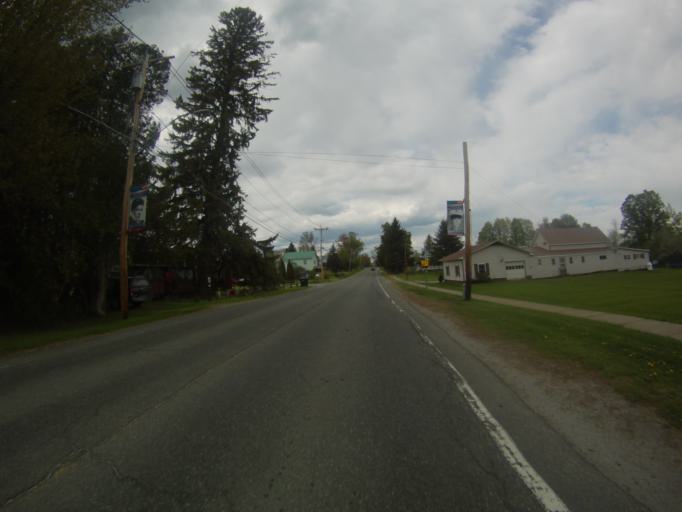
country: US
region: New York
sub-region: Essex County
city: Mineville
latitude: 44.0484
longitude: -73.5065
